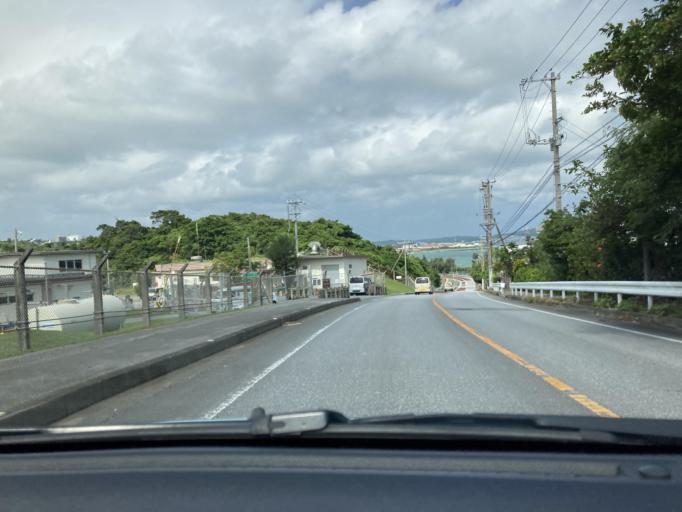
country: JP
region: Okinawa
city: Ishikawa
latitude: 26.4023
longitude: 127.8455
